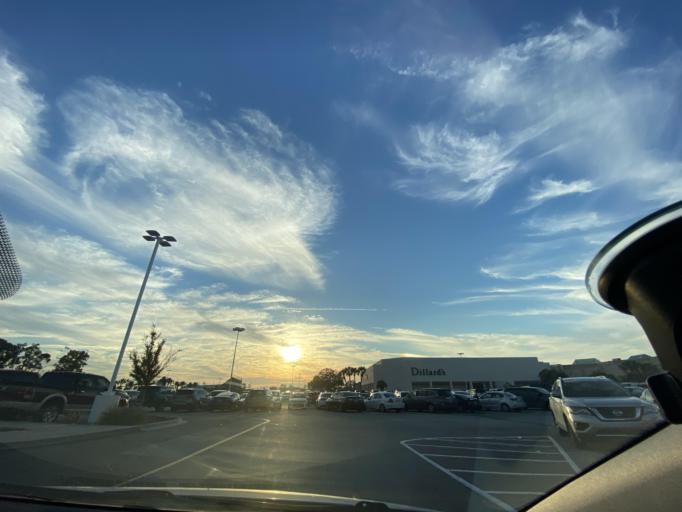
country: US
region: Florida
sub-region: Volusia County
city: Daytona Beach
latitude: 29.1965
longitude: -81.0616
